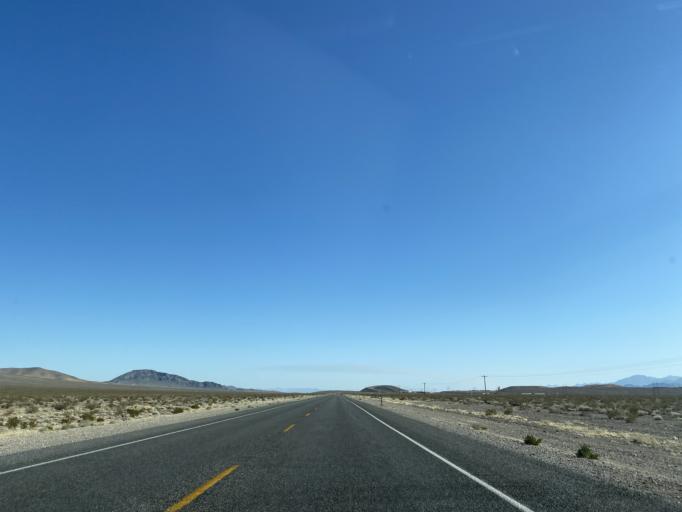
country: US
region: Nevada
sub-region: Nye County
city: Beatty
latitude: 36.7835
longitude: -116.6975
